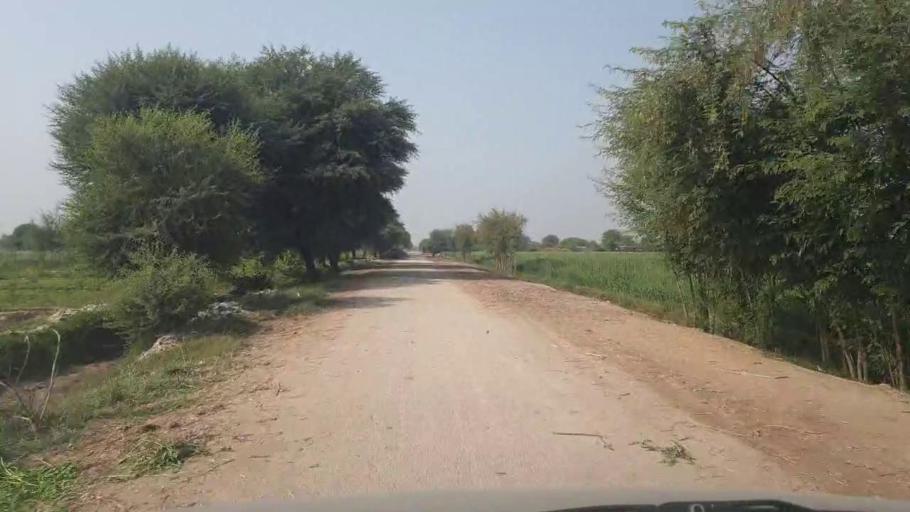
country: PK
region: Sindh
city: Umarkot
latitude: 25.4054
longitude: 69.7161
